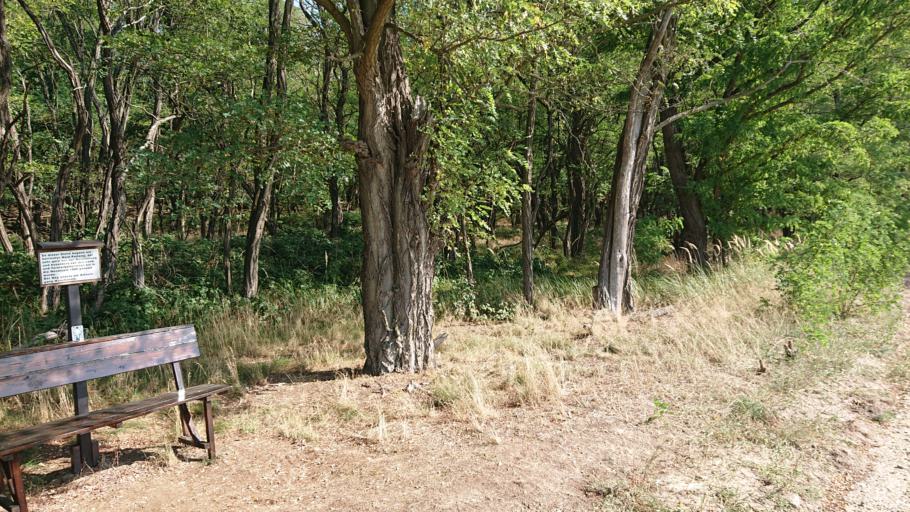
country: DE
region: Brandenburg
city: Munchehofe
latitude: 52.1373
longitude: 13.8461
